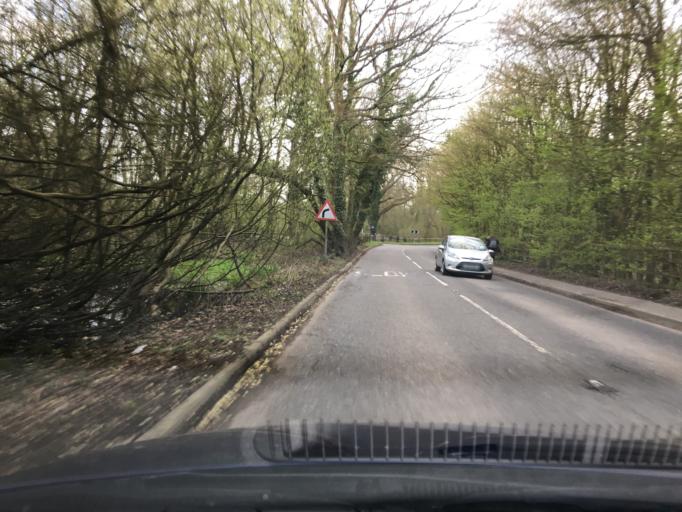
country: GB
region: England
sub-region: Hampshire
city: Yateley
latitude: 51.3473
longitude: -0.8149
